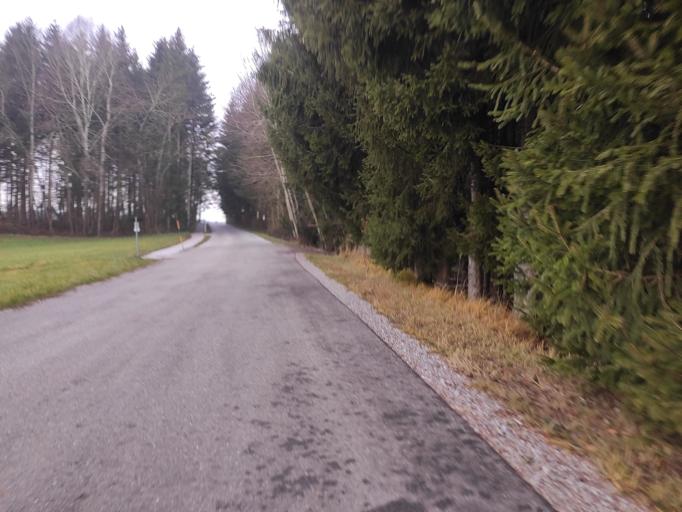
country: AT
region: Salzburg
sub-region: Politischer Bezirk Salzburg-Umgebung
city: Berndorf bei Salzburg
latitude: 48.0032
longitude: 13.0897
